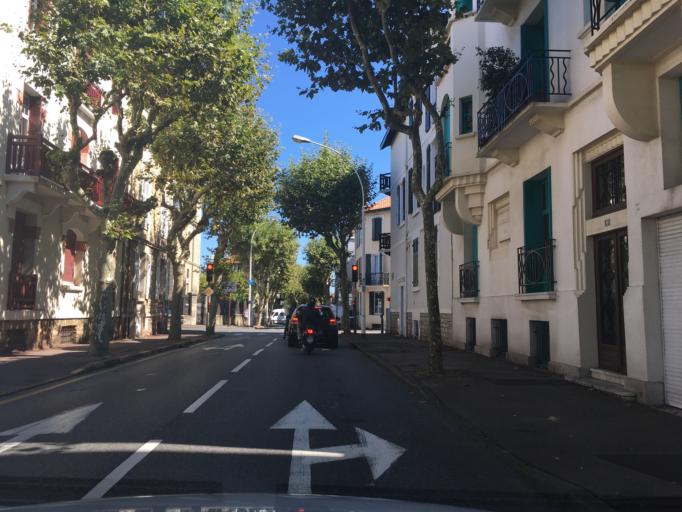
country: FR
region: Aquitaine
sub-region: Departement des Pyrenees-Atlantiques
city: Biarritz
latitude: 43.4785
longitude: -1.5627
